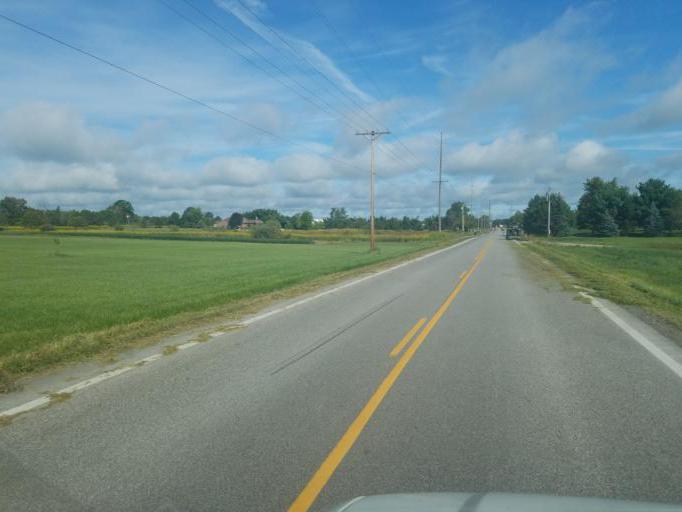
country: US
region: Ohio
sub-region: Wayne County
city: West Salem
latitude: 41.0132
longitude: -82.1190
